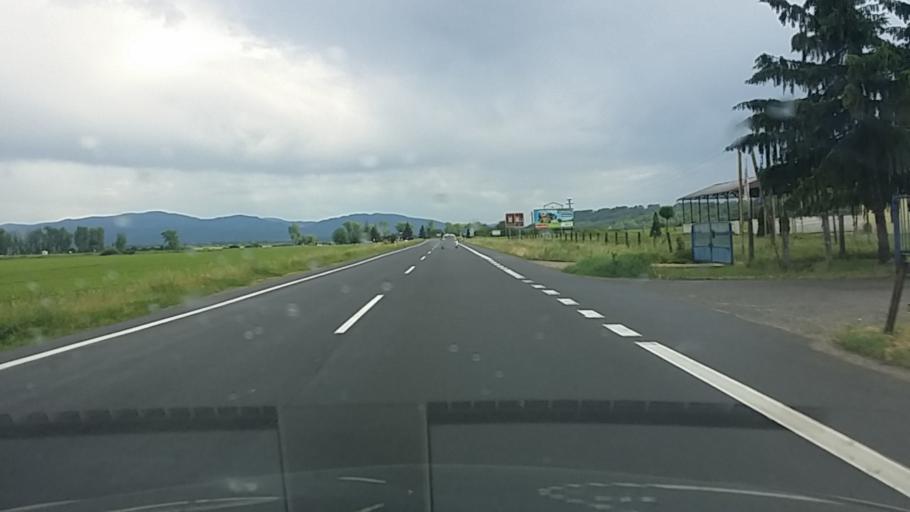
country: SK
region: Banskobystricky
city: Dudince
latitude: 48.1179
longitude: 18.8773
